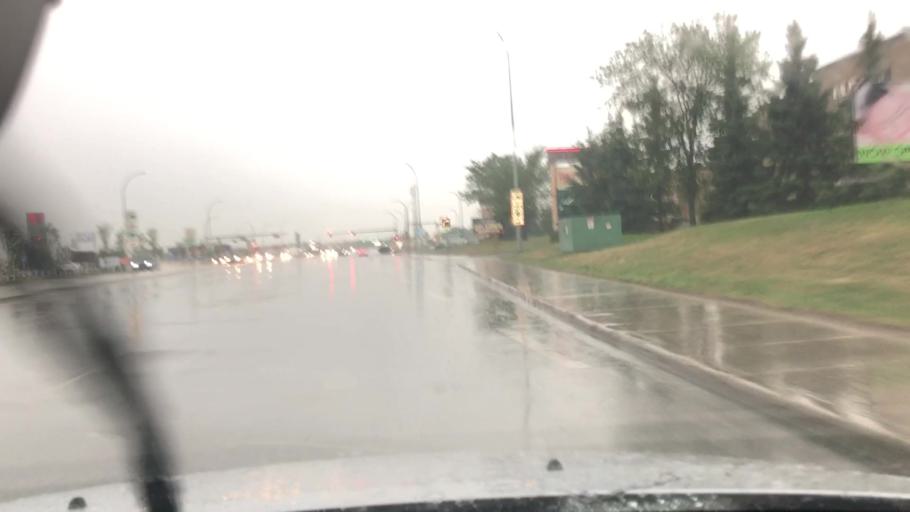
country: CA
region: Alberta
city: St. Albert
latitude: 53.5978
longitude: -113.5733
